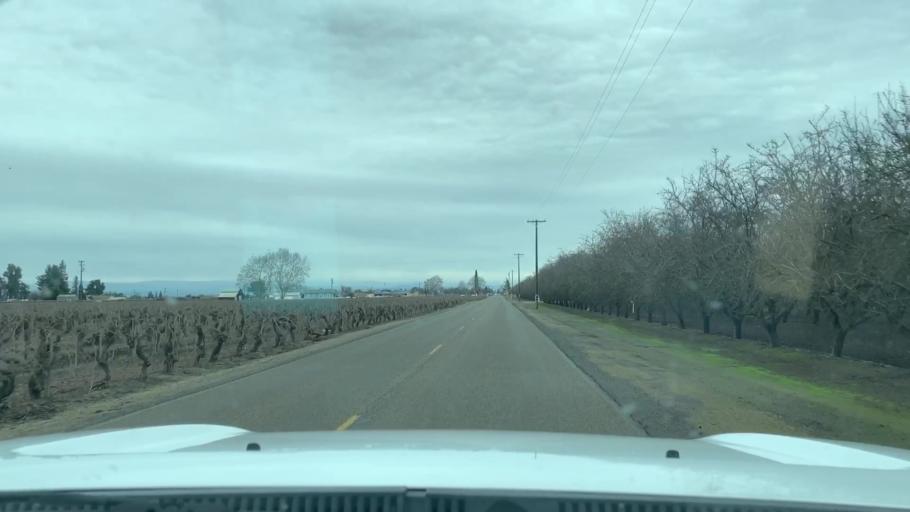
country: US
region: California
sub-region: Fresno County
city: Selma
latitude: 36.5471
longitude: -119.6894
